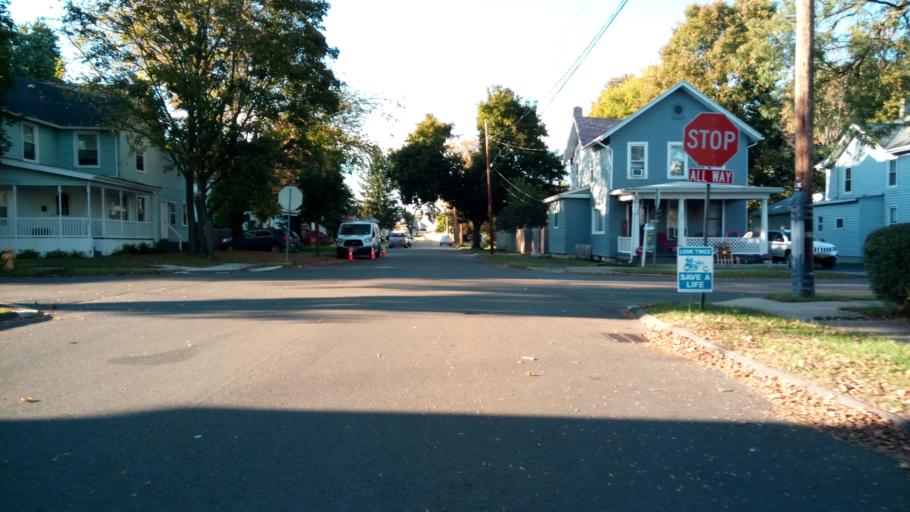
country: US
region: New York
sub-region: Chemung County
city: Elmira
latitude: 42.0728
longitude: -76.8107
